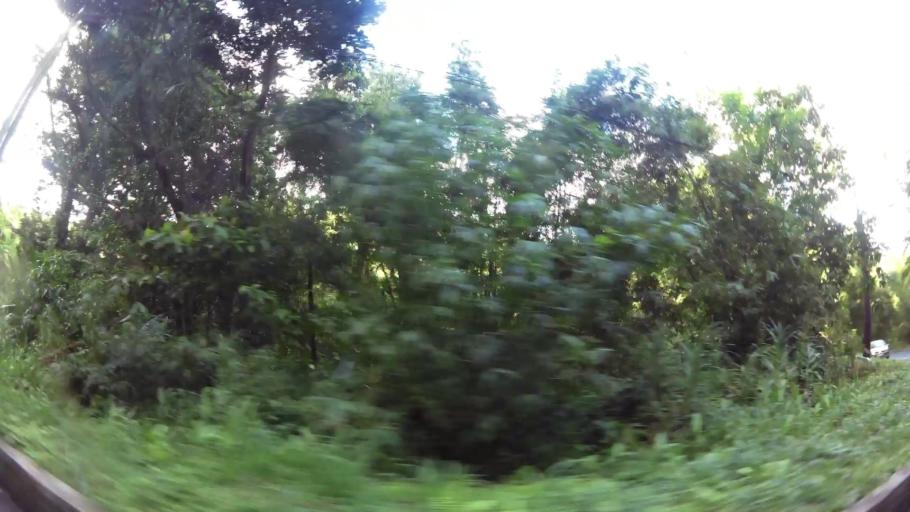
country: MQ
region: Martinique
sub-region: Martinique
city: Saint-Joseph
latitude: 14.6900
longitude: -61.0873
